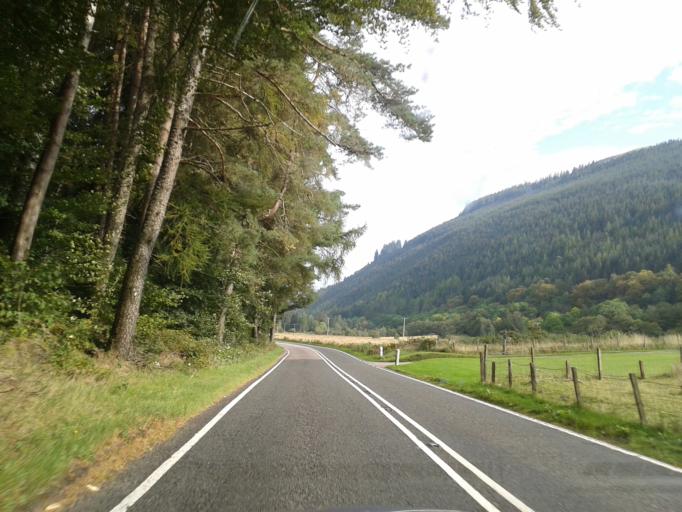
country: GB
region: Scotland
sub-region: Highland
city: Spean Bridge
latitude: 57.0389
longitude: -4.8077
